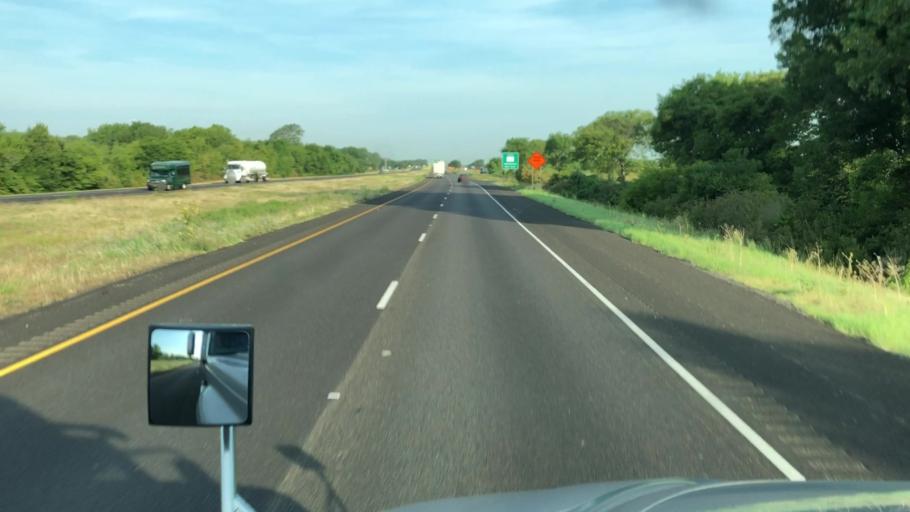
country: US
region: Texas
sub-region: McLennan County
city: Bellmead
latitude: 31.5437
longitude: -97.0569
